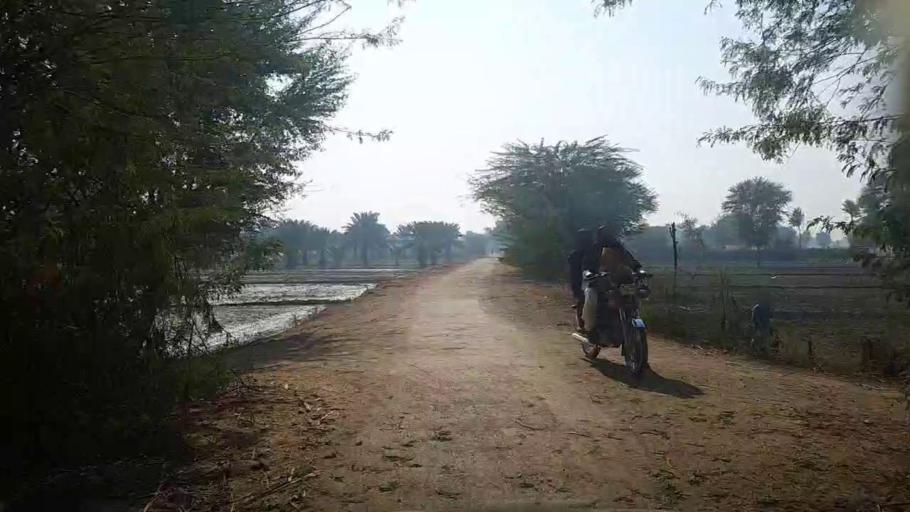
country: PK
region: Sindh
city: Kandiari
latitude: 26.9768
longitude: 68.4694
